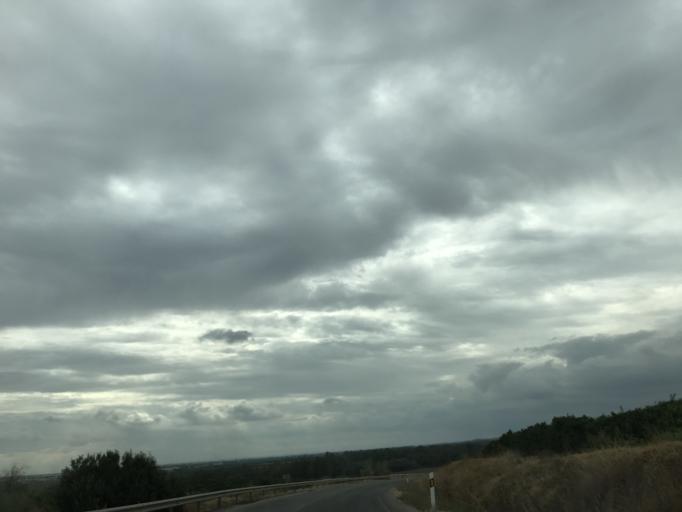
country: ES
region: Andalusia
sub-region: Provincia de Sevilla
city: Villanueva del Rio y Minas
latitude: 37.6355
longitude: -5.7038
